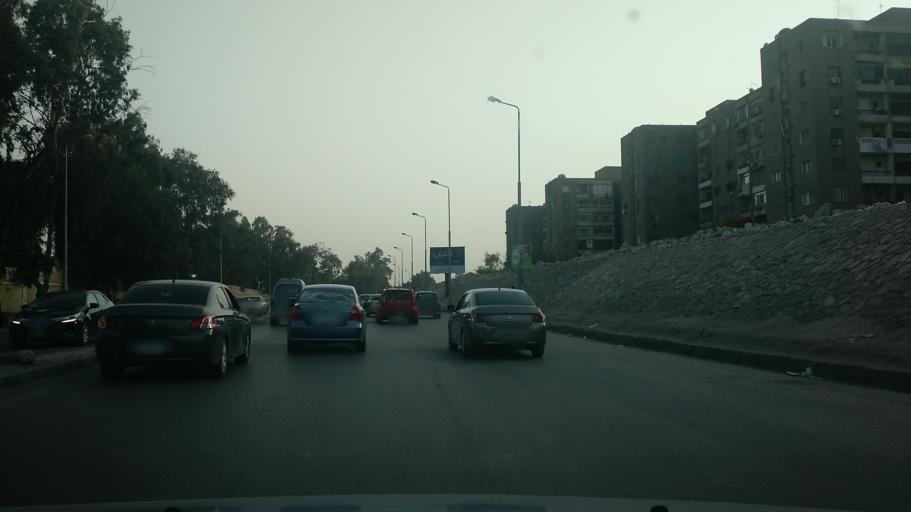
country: EG
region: Al Jizah
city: Al Jizah
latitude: 29.9844
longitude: 31.1230
